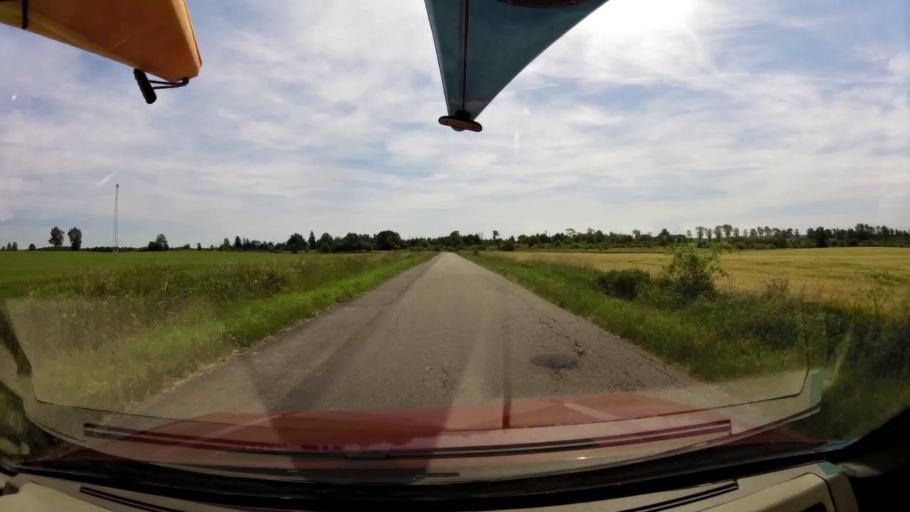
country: PL
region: West Pomeranian Voivodeship
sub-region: Powiat slawienski
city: Darlowo
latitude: 54.3207
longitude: 16.4026
